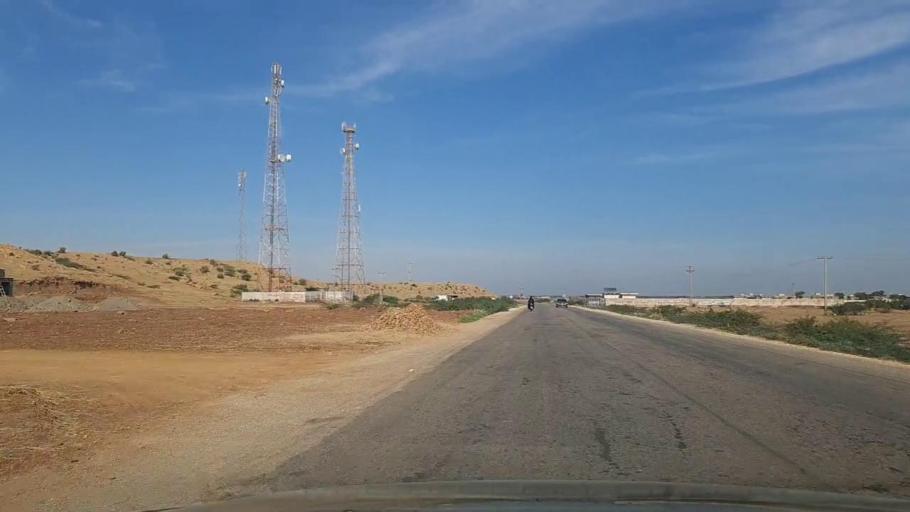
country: PK
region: Sindh
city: Bulri
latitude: 25.0510
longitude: 68.2452
